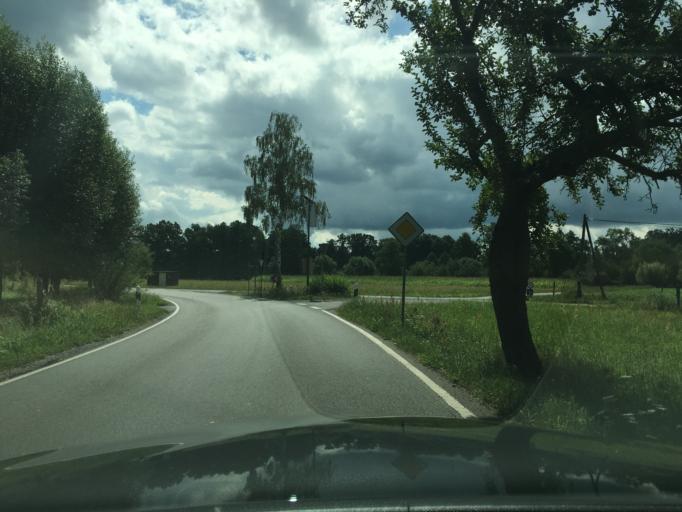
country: DE
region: Brandenburg
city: Burg
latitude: 51.8461
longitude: 14.1035
